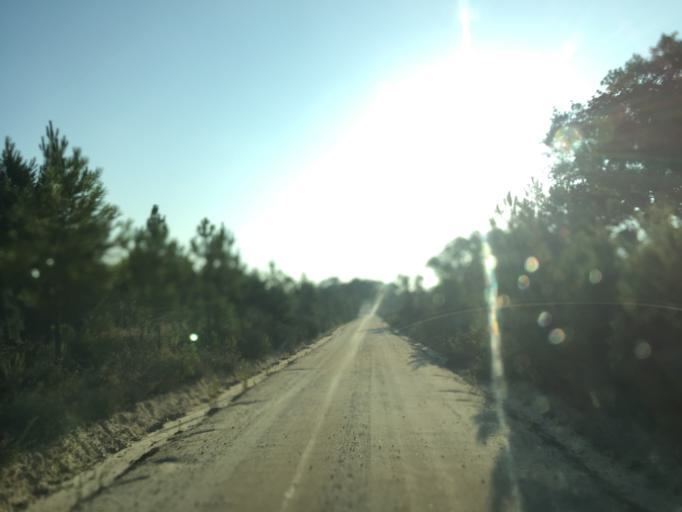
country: PT
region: Portalegre
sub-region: Ponte de Sor
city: Santo Andre
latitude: 39.1648
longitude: -8.2875
